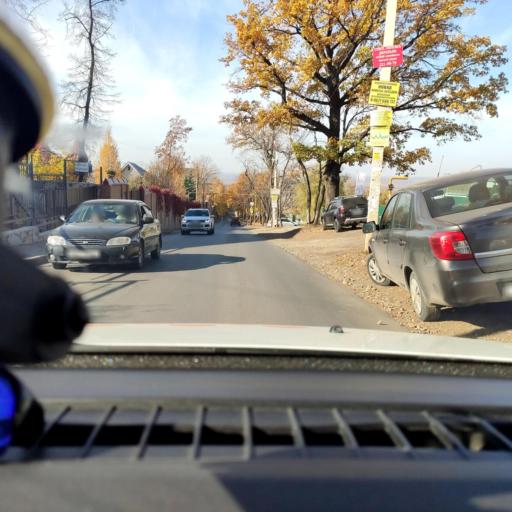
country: RU
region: Samara
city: Samara
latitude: 53.2591
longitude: 50.2052
